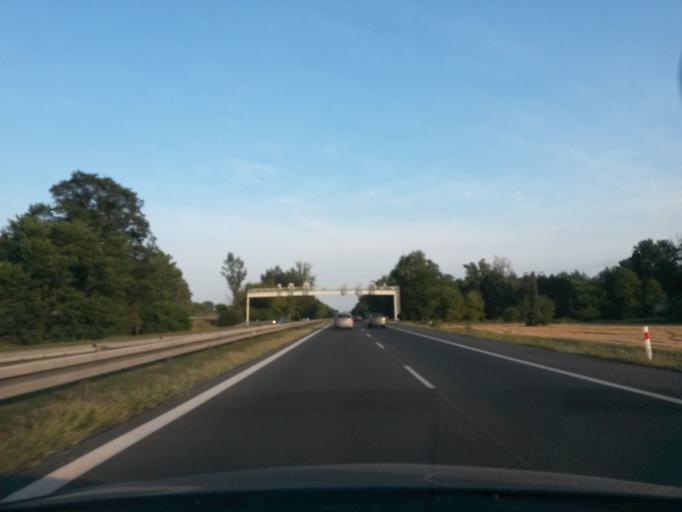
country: PL
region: Masovian Voivodeship
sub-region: Powiat nowodworski
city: Nowy Dwor Mazowiecki
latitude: 52.4071
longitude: 20.7025
